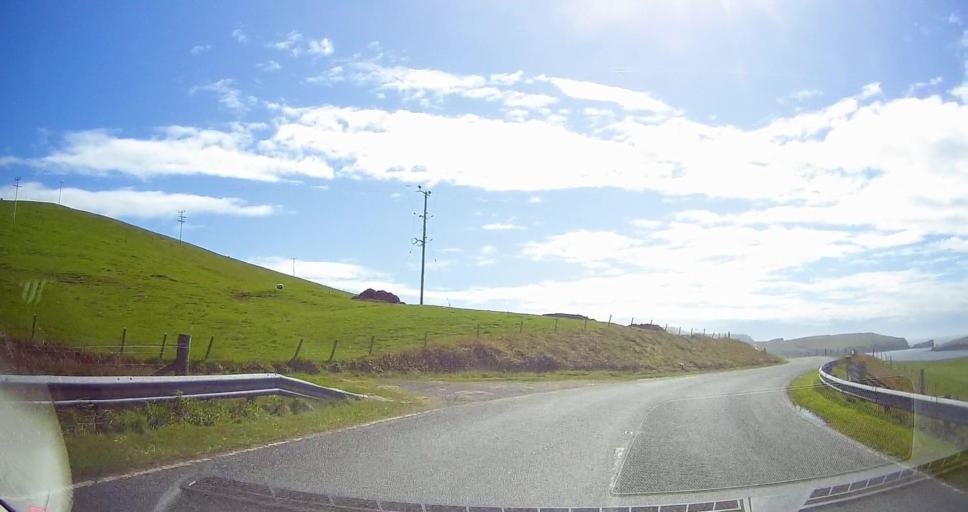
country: GB
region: Scotland
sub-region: Shetland Islands
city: Sandwick
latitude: 59.9591
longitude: -1.3248
